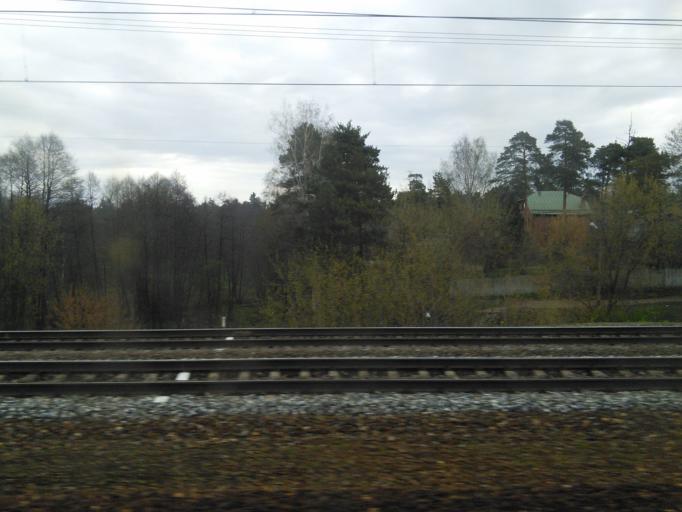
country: RU
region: Moskovskaya
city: Kratovo
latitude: 55.5937
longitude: 38.1560
